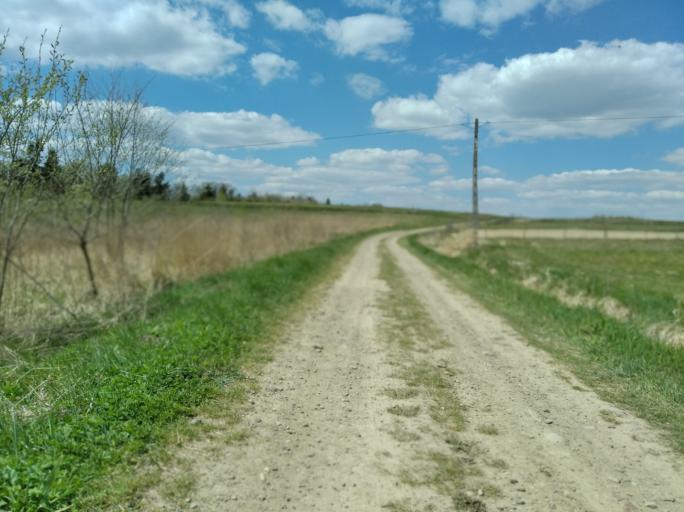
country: PL
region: Subcarpathian Voivodeship
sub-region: Powiat brzozowski
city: Jablonka
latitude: 49.7412
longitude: 22.0872
